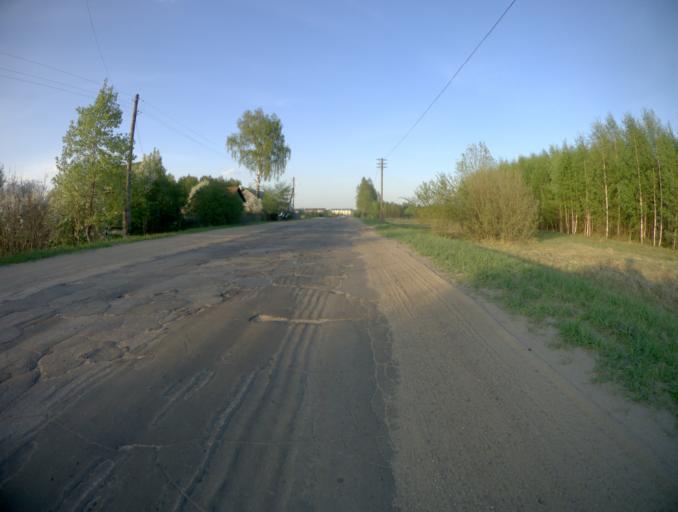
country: RU
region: Ivanovo
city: Yuzha
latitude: 56.5763
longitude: 41.9776
